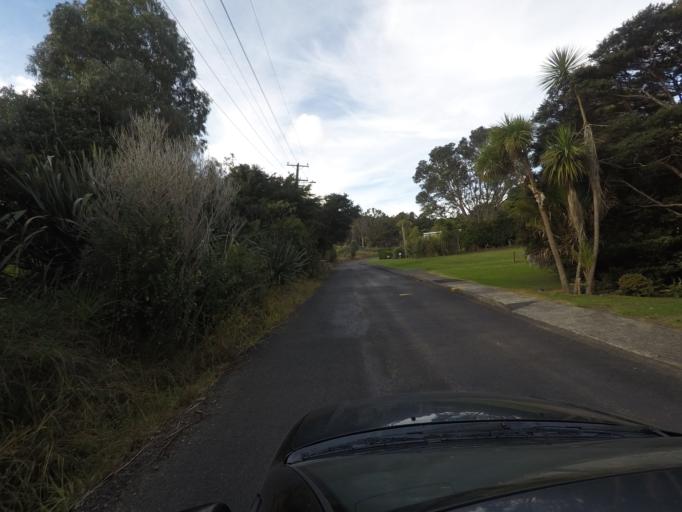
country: NZ
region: Auckland
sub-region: Auckland
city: Titirangi
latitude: -36.9979
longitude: 174.5724
